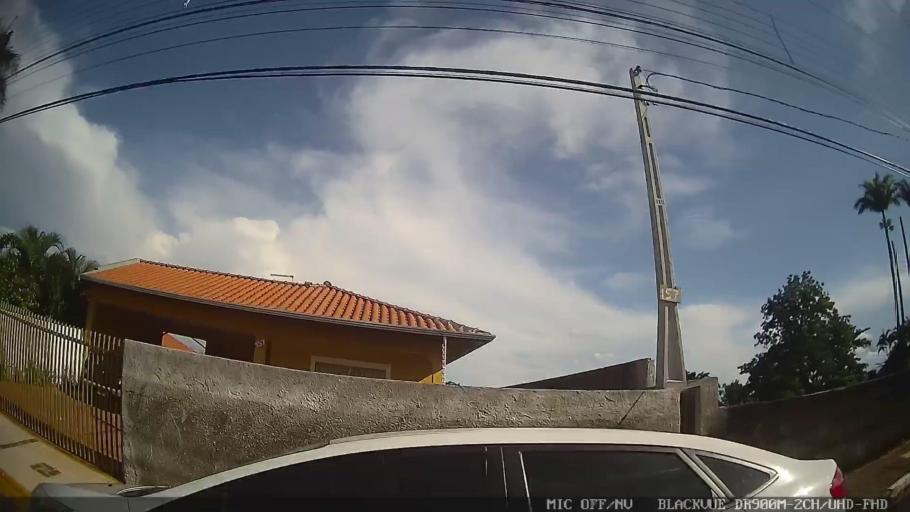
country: BR
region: Sao Paulo
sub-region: Laranjal Paulista
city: Laranjal Paulista
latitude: -23.0847
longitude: -47.7905
